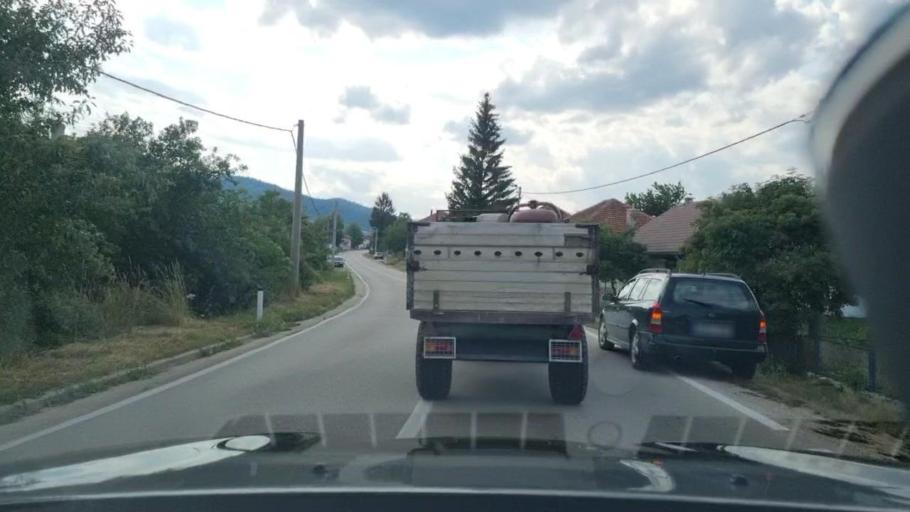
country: BA
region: Federation of Bosnia and Herzegovina
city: Glamoc
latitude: 44.0459
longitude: 16.8615
